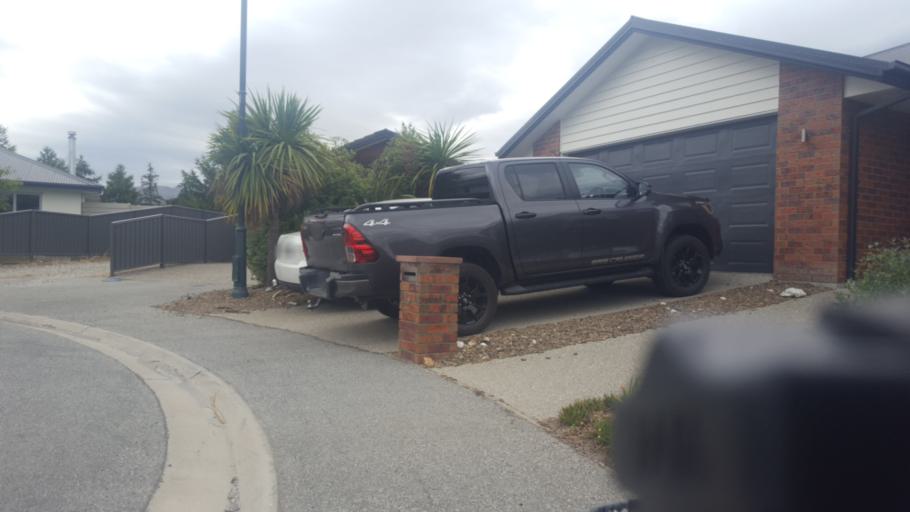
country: NZ
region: Otago
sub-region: Queenstown-Lakes District
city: Wanaka
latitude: -45.0478
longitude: 169.1864
